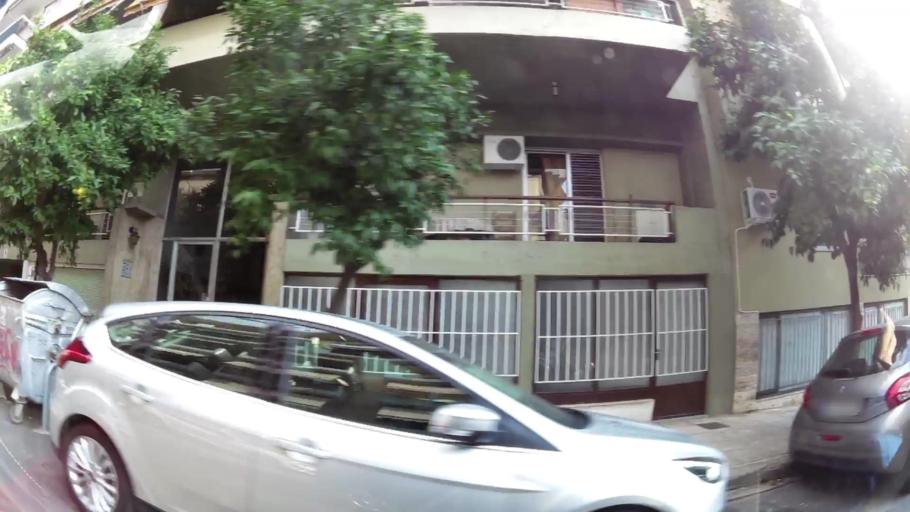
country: GR
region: Attica
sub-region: Nomarchia Athinas
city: Nea Smyrni
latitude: 37.9589
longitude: 23.7116
